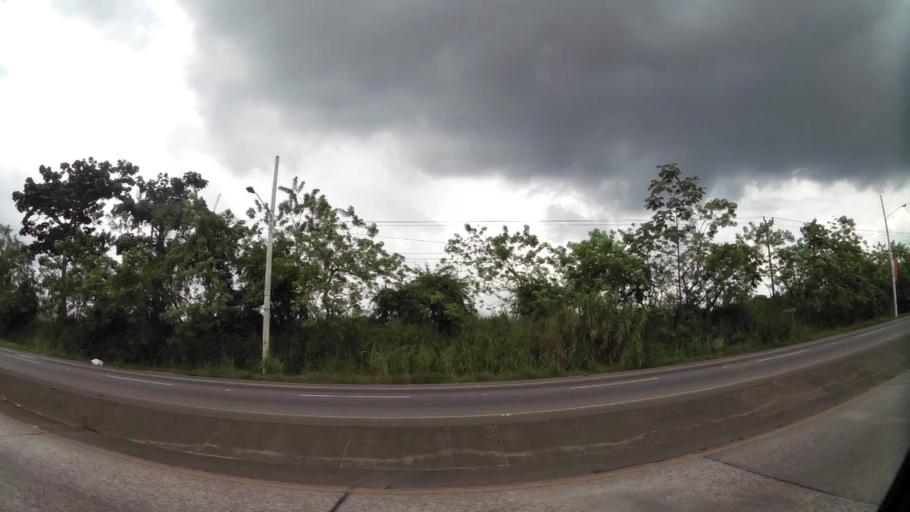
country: PA
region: Panama
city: Cabra Numero Uno
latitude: 9.1010
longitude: -79.3384
